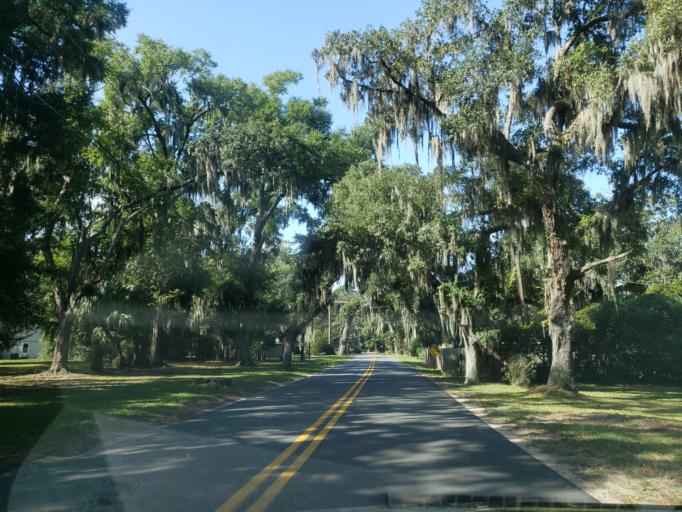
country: US
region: Georgia
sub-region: Chatham County
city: Montgomery
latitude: 31.9317
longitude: -81.0961
